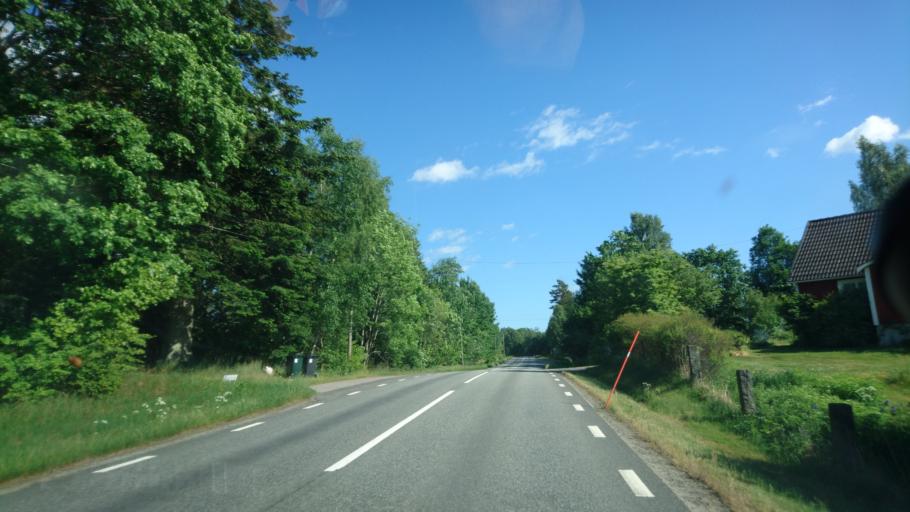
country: SE
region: Kronoberg
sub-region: Almhults Kommun
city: AElmhult
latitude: 56.4790
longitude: 14.2085
